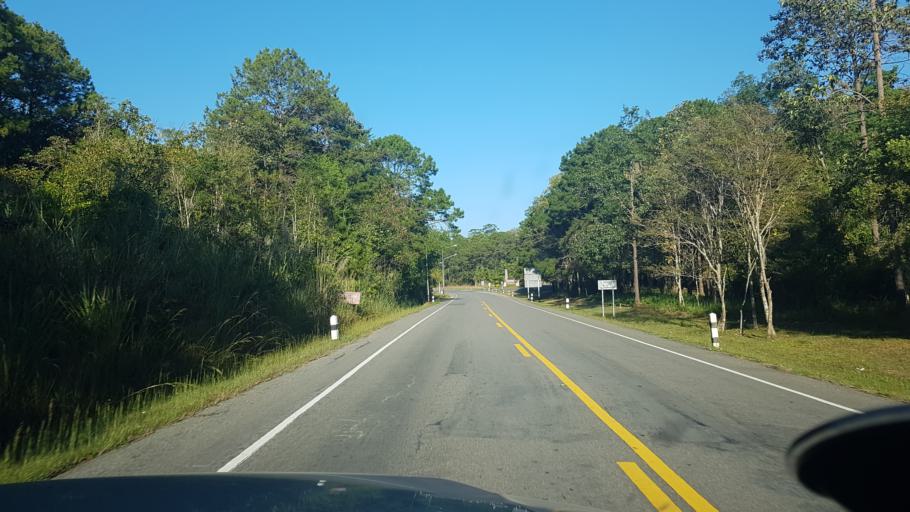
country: TH
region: Phetchabun
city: Nam Nao
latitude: 16.7288
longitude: 101.5626
